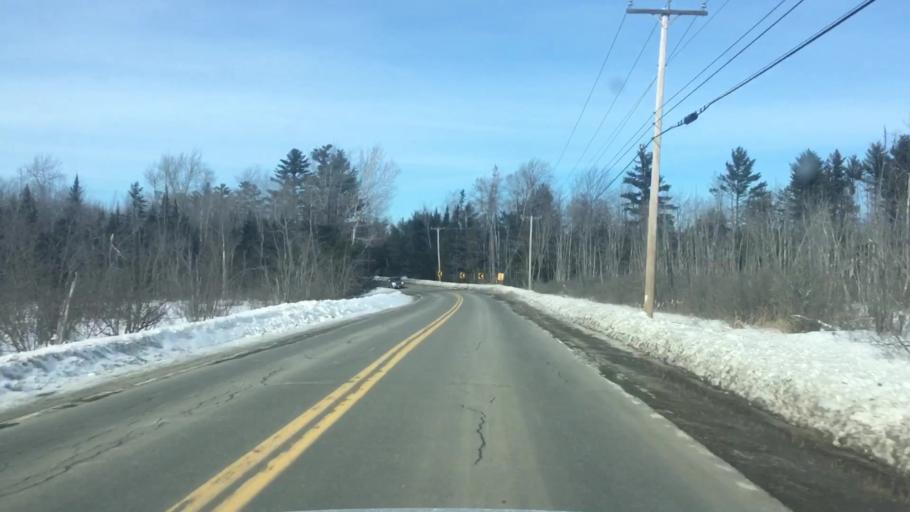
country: US
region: Maine
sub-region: Penobscot County
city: Charleston
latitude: 45.0447
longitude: -69.0294
